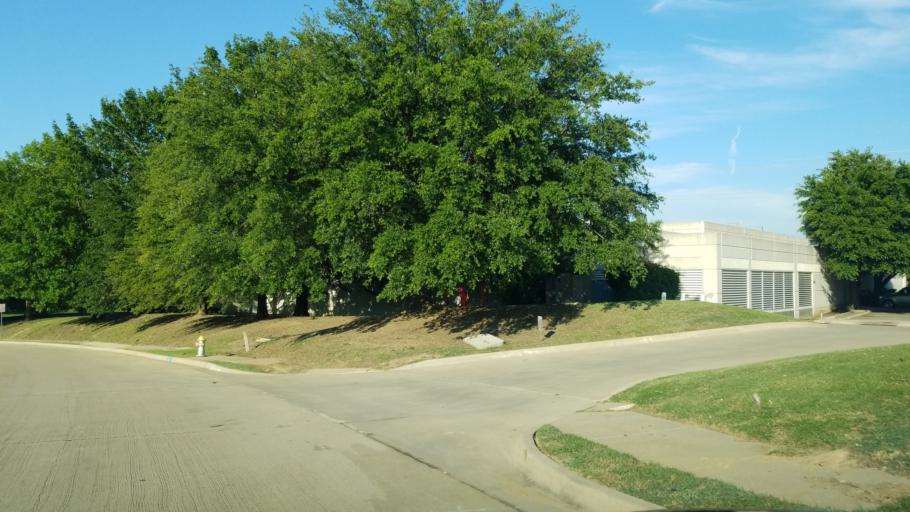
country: US
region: Texas
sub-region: Dallas County
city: Coppell
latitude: 32.9105
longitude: -96.9926
